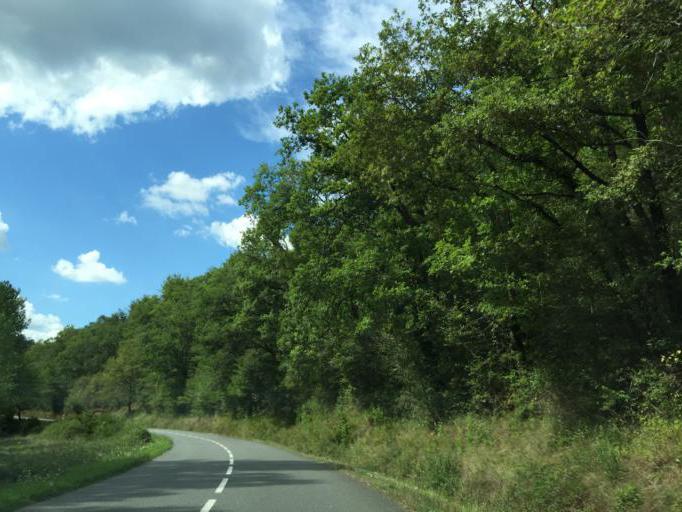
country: FR
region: Midi-Pyrenees
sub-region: Departement de l'Aveyron
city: Marcillac-Vallon
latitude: 44.4975
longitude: 2.4370
